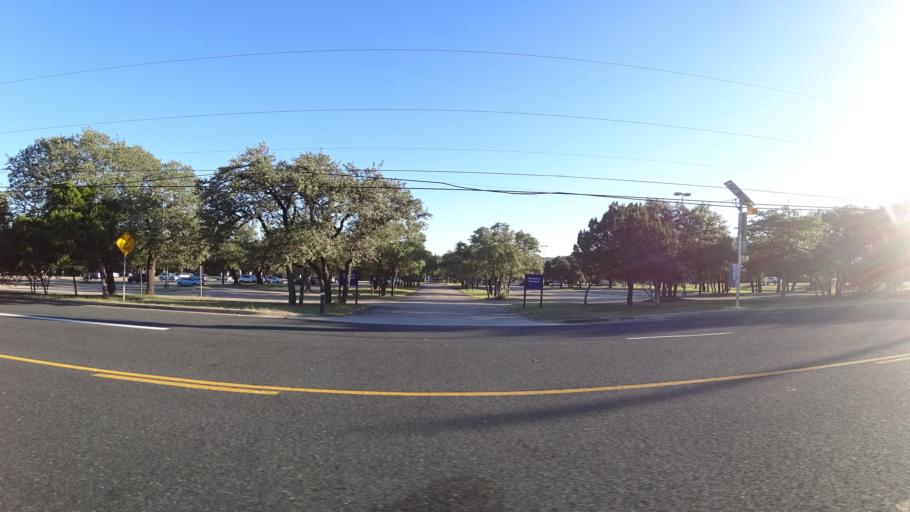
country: US
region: Texas
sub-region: Travis County
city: West Lake Hills
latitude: 30.3399
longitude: -97.8046
